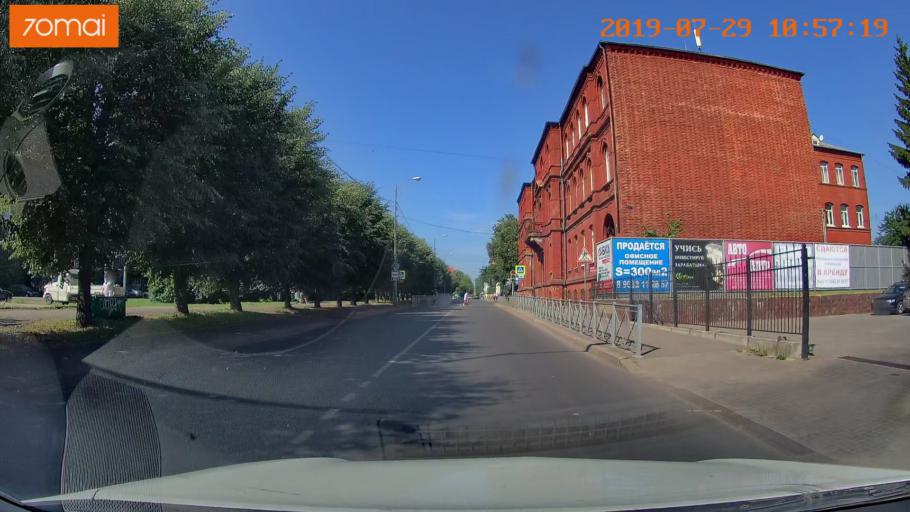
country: RU
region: Kaliningrad
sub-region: Gorod Kaliningrad
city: Kaliningrad
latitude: 54.7137
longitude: 20.5351
